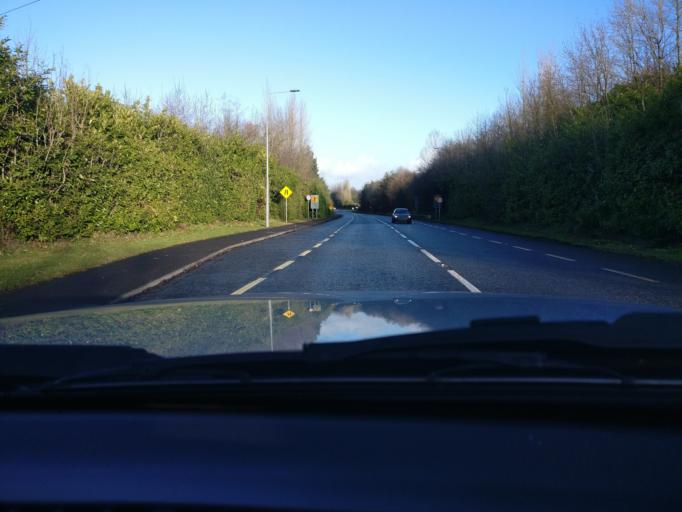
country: IE
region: Leinster
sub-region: An Iarmhi
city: An Muileann gCearr
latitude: 53.5359
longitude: -7.3094
